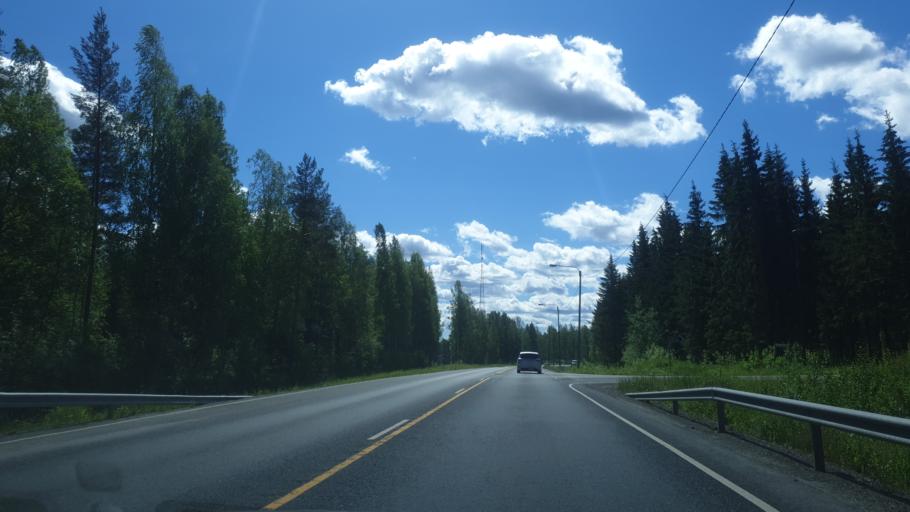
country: FI
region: Northern Savo
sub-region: Varkaus
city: Leppaevirta
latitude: 62.5860
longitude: 27.6052
